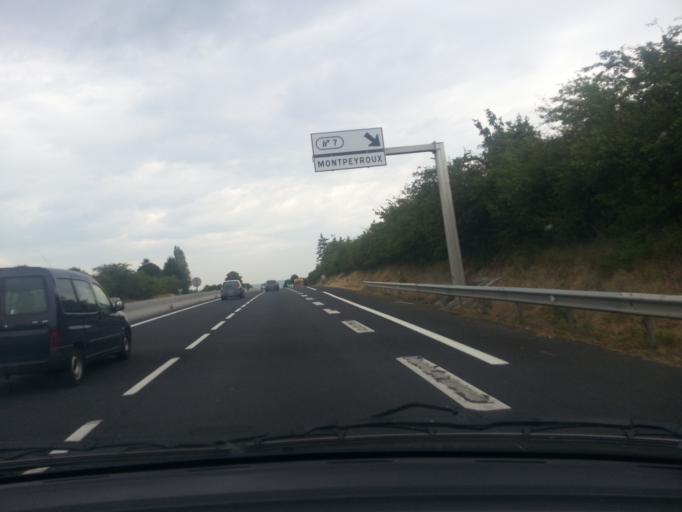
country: FR
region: Auvergne
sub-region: Departement du Puy-de-Dome
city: Plauzat
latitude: 45.6208
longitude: 3.1983
